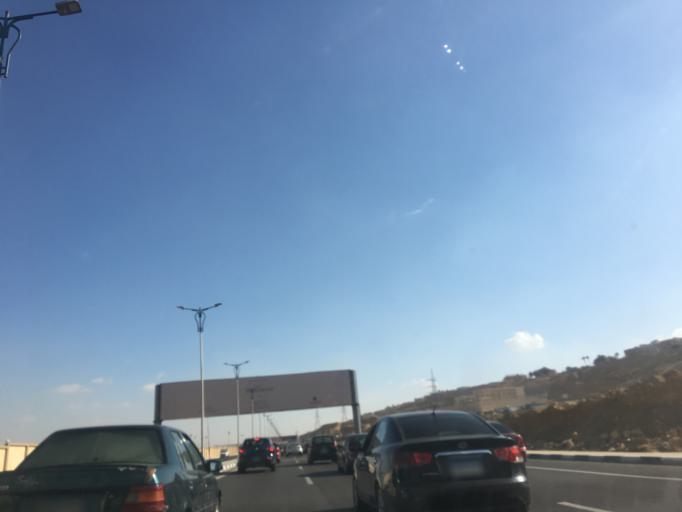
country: EG
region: Muhafazat al Qahirah
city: Cairo
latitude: 30.0245
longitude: 31.3243
